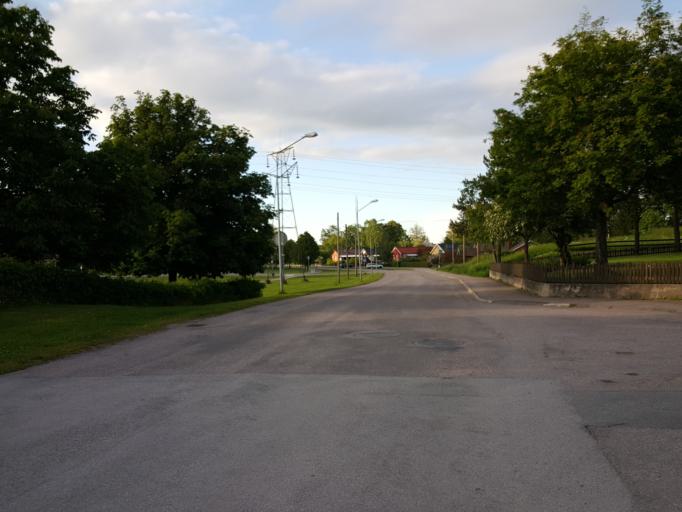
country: SE
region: Uppsala
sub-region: Osthammars Kommun
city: Gimo
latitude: 60.1693
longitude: 18.1840
